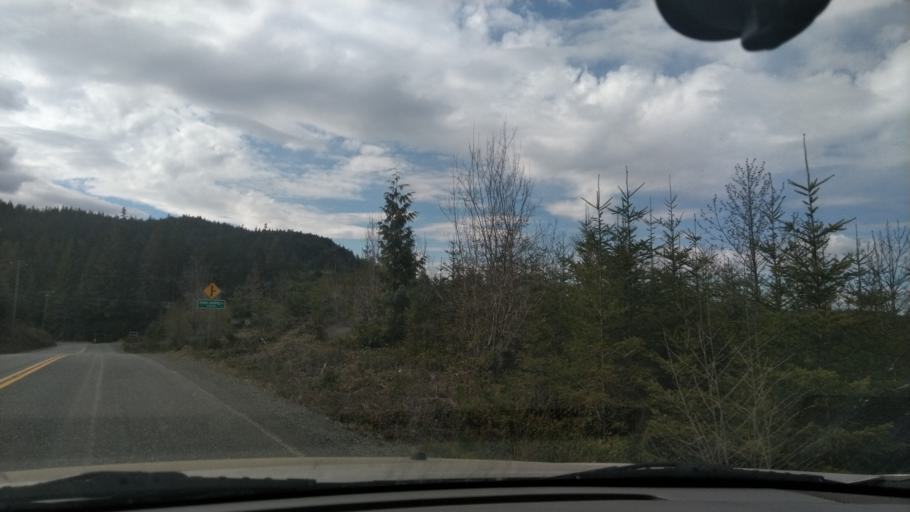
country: CA
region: British Columbia
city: Campbell River
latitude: 49.9986
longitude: -125.3769
